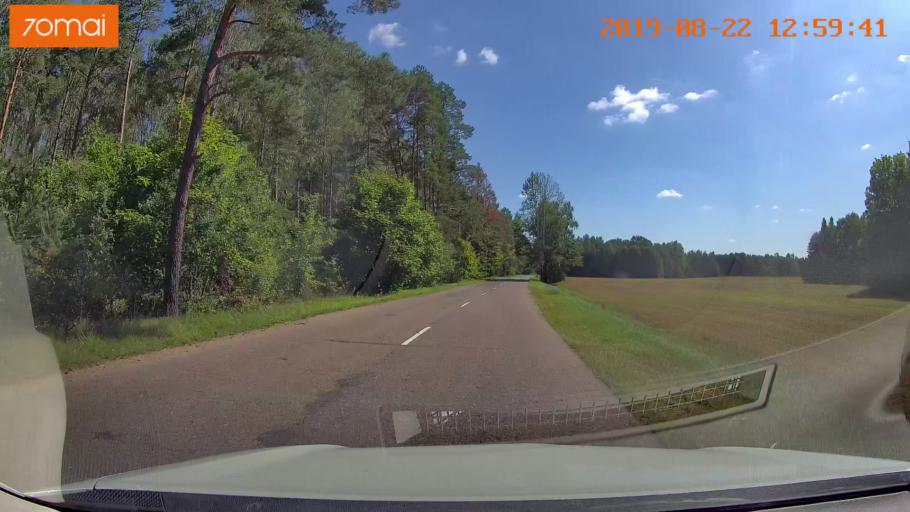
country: BY
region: Minsk
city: Prawdzinski
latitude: 53.4224
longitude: 27.7963
